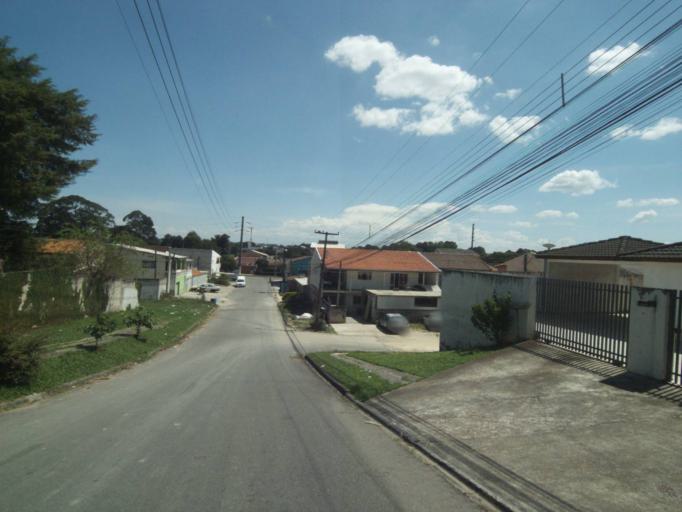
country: BR
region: Parana
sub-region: Curitiba
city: Curitiba
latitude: -25.4682
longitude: -49.2460
